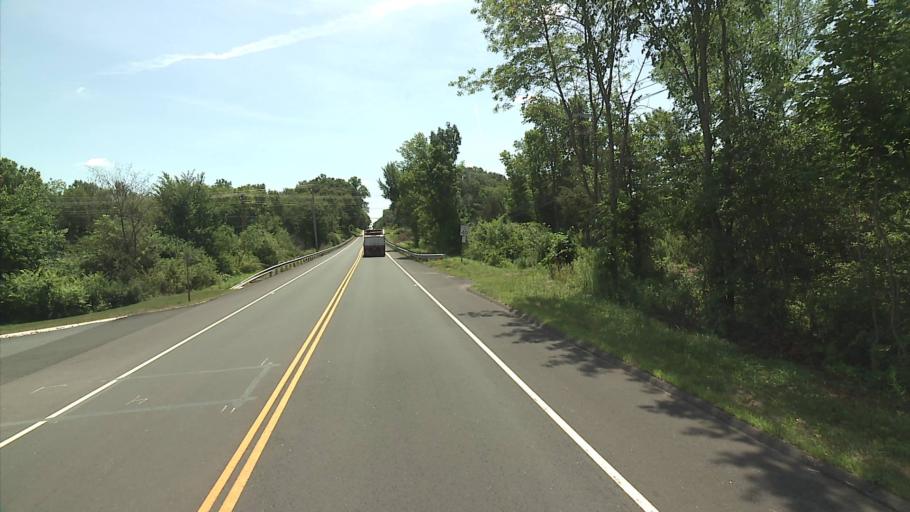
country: US
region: Connecticut
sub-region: Hartford County
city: Kensington
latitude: 41.6155
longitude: -72.7273
